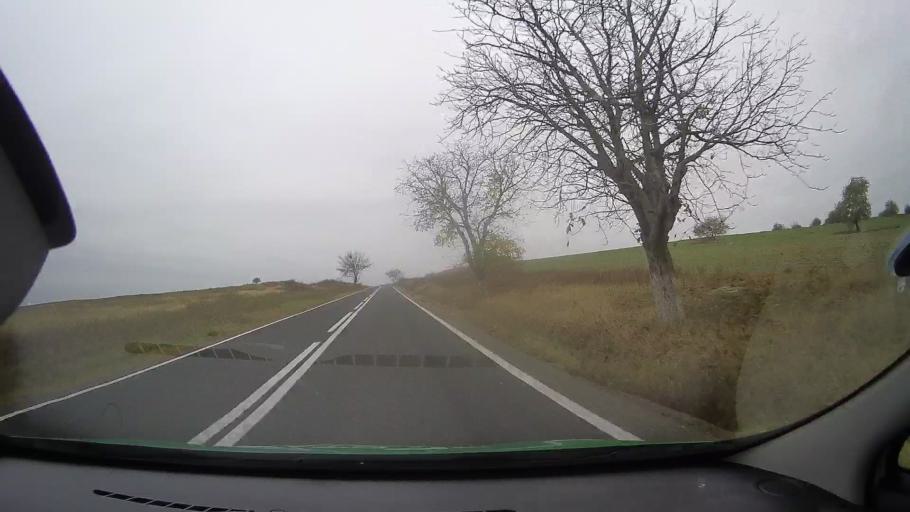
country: RO
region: Constanta
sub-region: Comuna Ghindaresti
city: Ghindaresti
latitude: 44.7062
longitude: 28.0516
